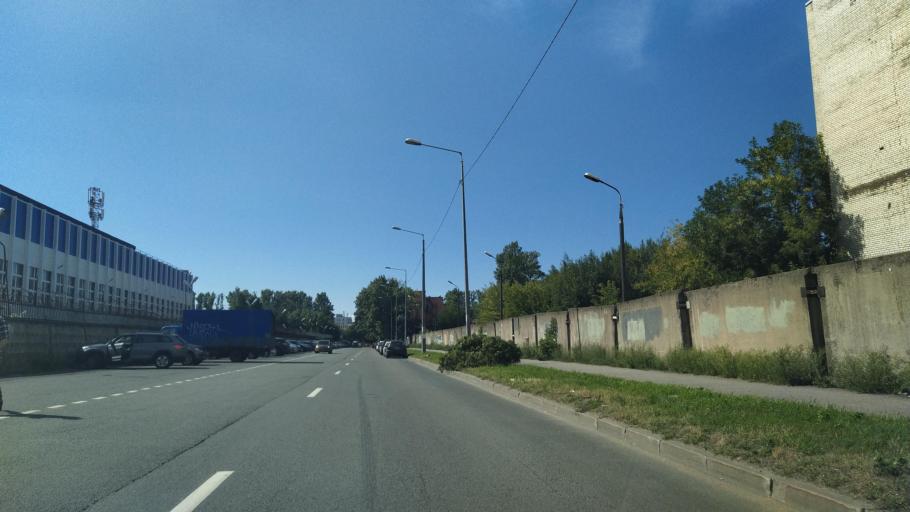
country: RU
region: Leningrad
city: Finlyandskiy
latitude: 59.9746
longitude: 30.3563
